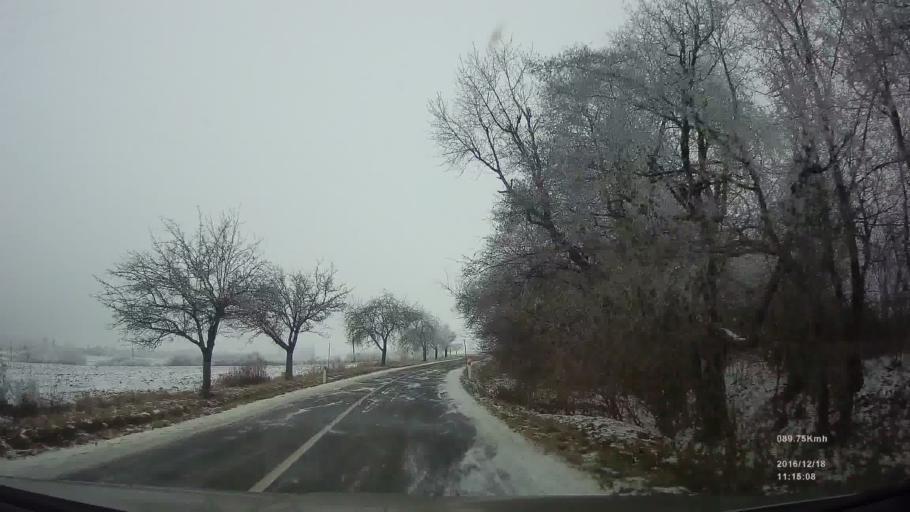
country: SK
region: Presovsky
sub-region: Okres Presov
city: Presov
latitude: 48.9014
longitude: 21.3224
